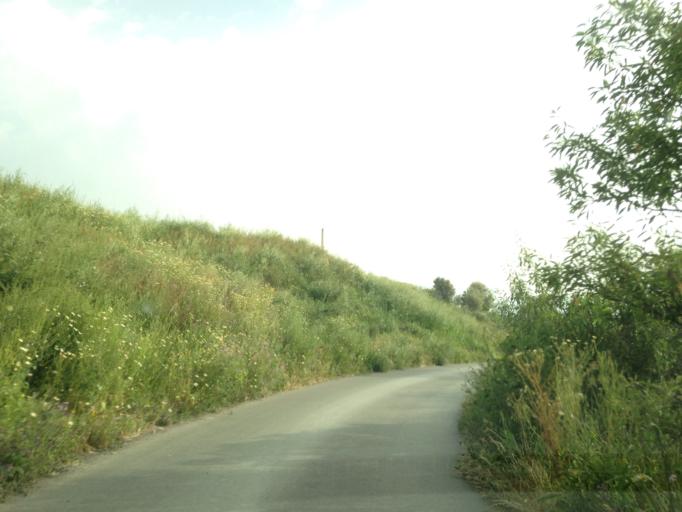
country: ES
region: Andalusia
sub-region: Provincia de Malaga
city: Estacion de Cartama
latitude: 36.7520
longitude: -4.5476
